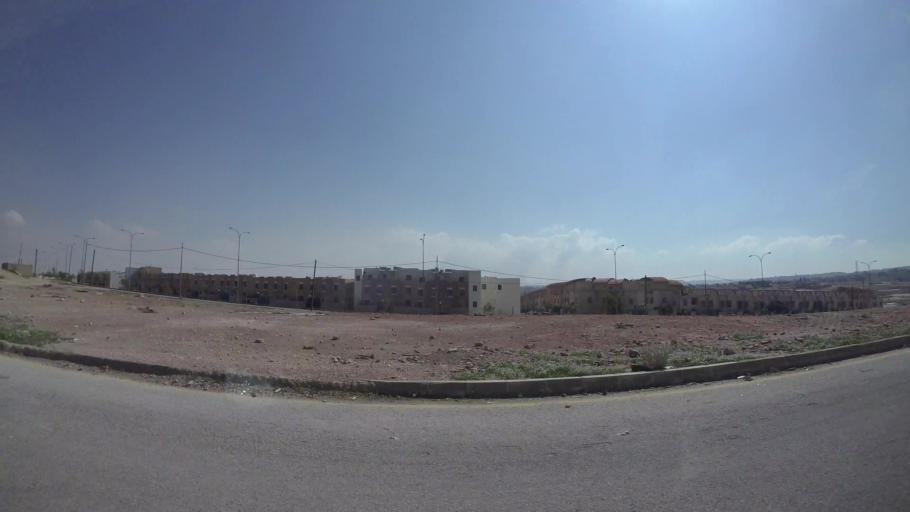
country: JO
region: Zarqa
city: Zarqa
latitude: 32.0738
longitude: 36.1092
